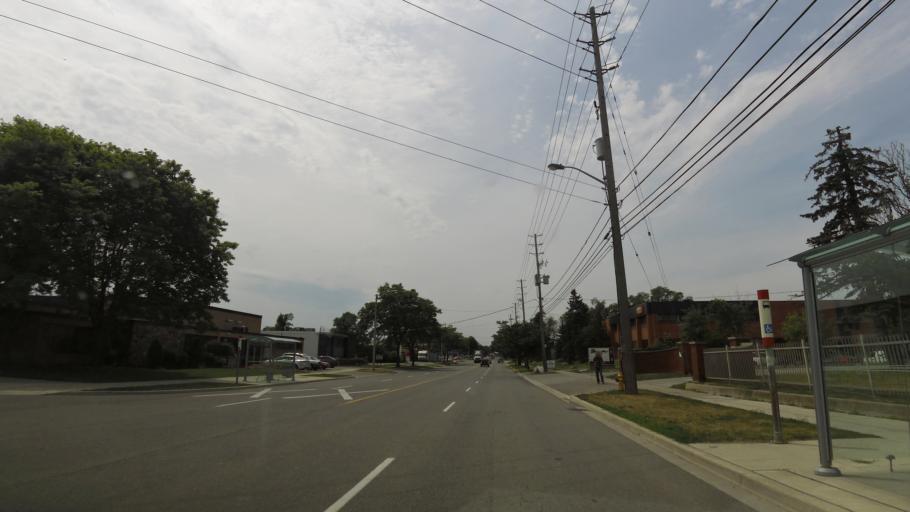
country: CA
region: Ontario
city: Etobicoke
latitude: 43.6060
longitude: -79.5265
